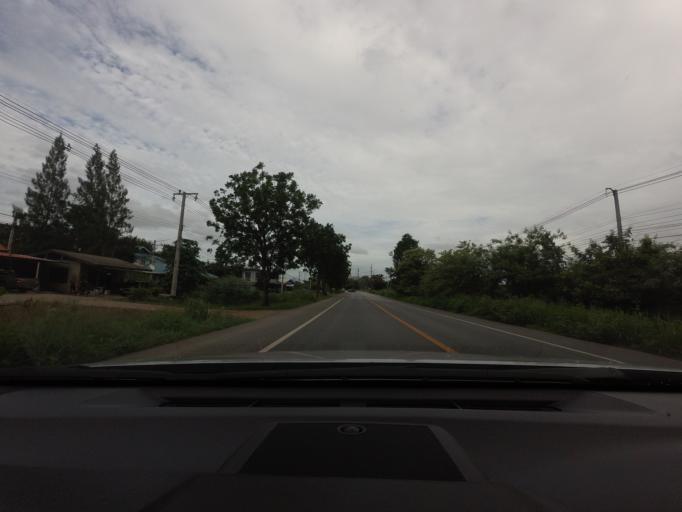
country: TH
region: Prachuap Khiri Khan
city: Hua Hin
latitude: 12.5789
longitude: 99.8611
